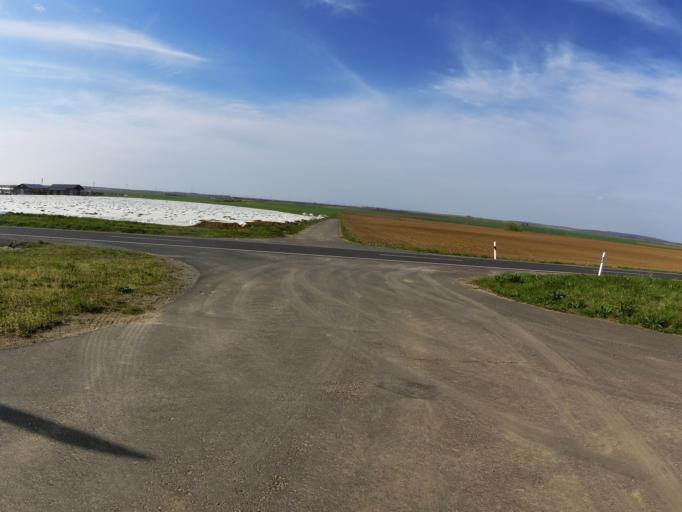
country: DE
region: Bavaria
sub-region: Regierungsbezirk Unterfranken
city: Mainstockheim
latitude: 49.7915
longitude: 10.1183
